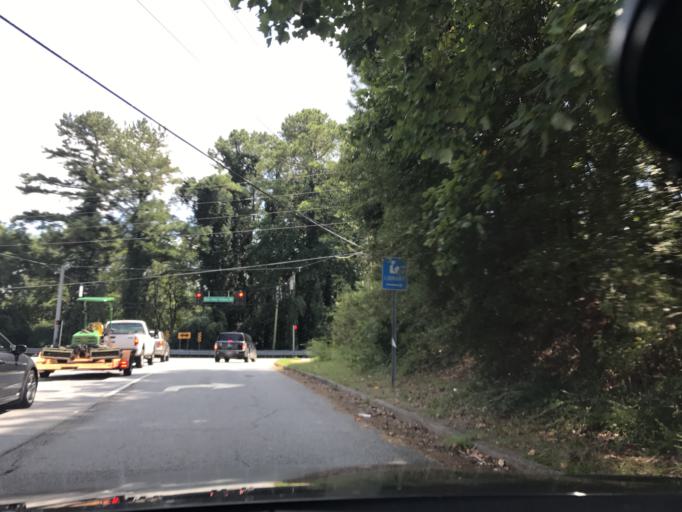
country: US
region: Georgia
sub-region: Gwinnett County
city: Mountain Park
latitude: 33.8526
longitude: -84.1119
